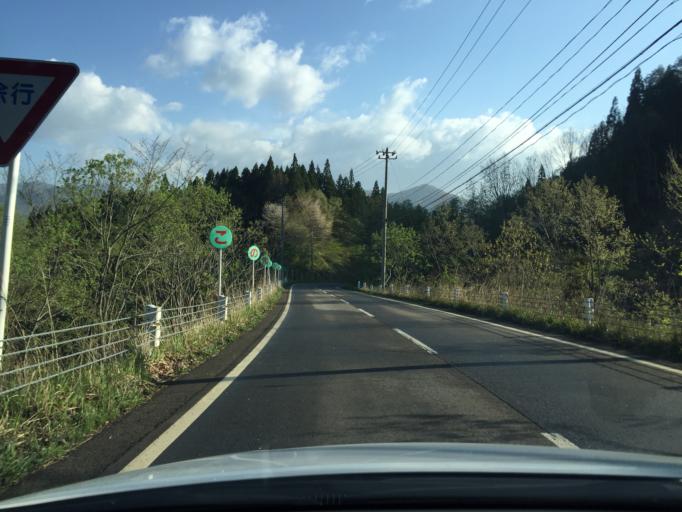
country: JP
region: Fukushima
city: Inawashiro
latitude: 37.6611
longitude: 140.0105
